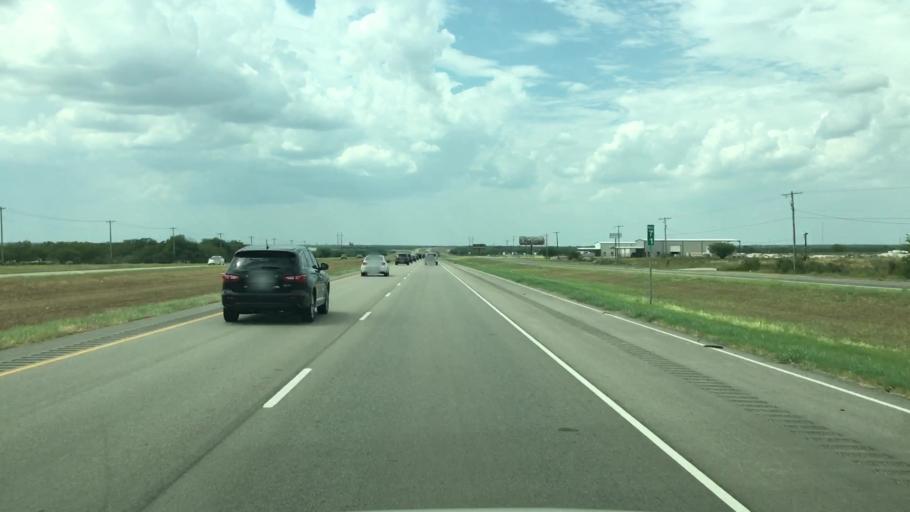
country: US
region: Texas
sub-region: Live Oak County
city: Three Rivers
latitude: 28.5072
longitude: -98.1640
